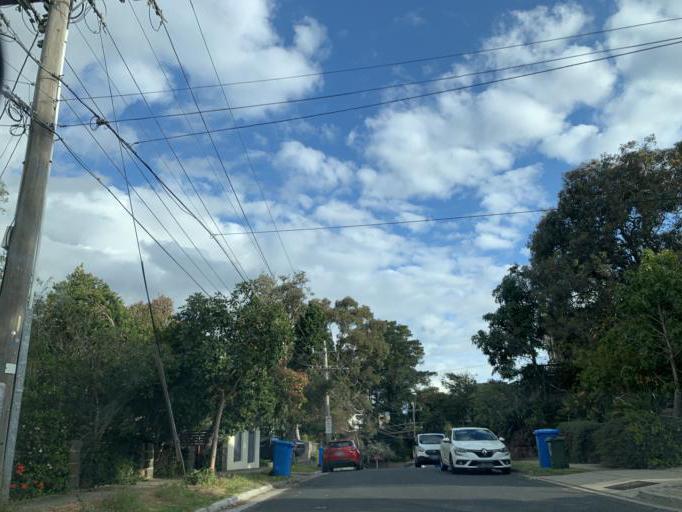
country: AU
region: Victoria
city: Beaumaris
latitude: -37.9762
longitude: 145.0284
